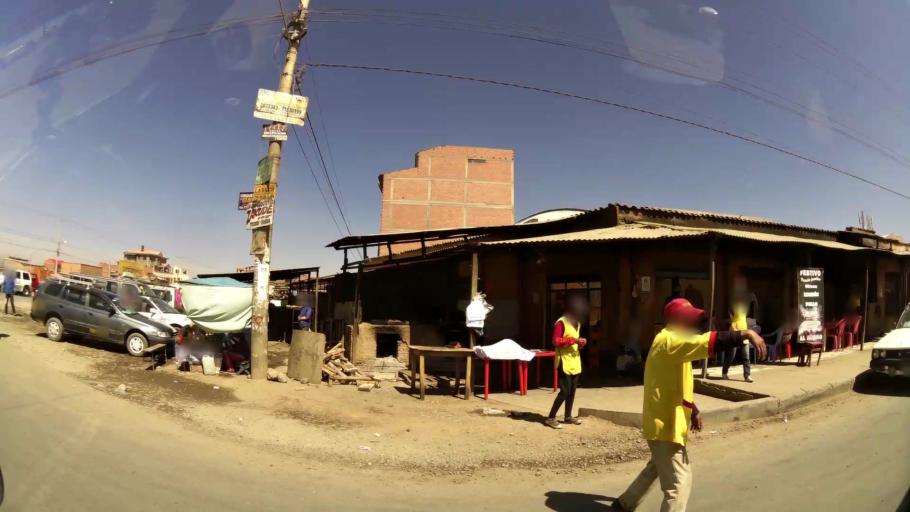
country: BO
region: La Paz
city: La Paz
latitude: -16.5426
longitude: -68.1985
